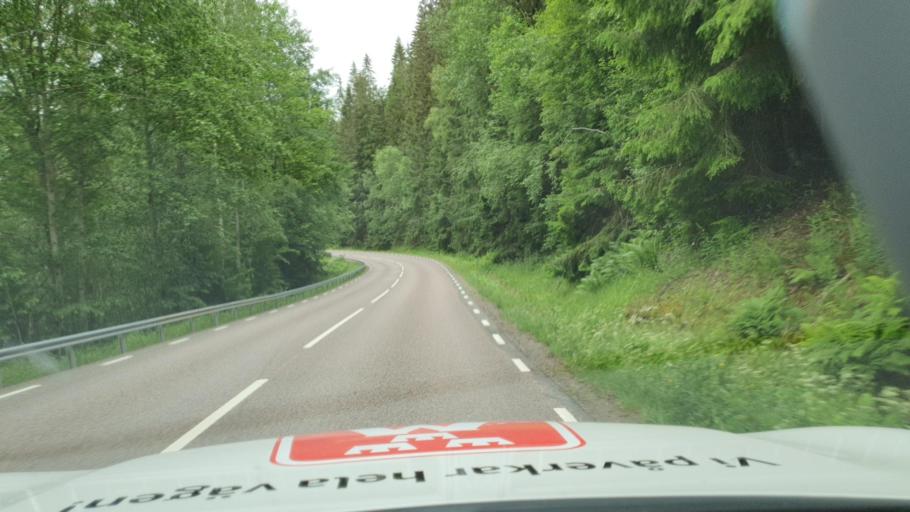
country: SE
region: Vaermland
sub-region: Sunne Kommun
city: Sunne
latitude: 59.8256
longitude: 12.9902
